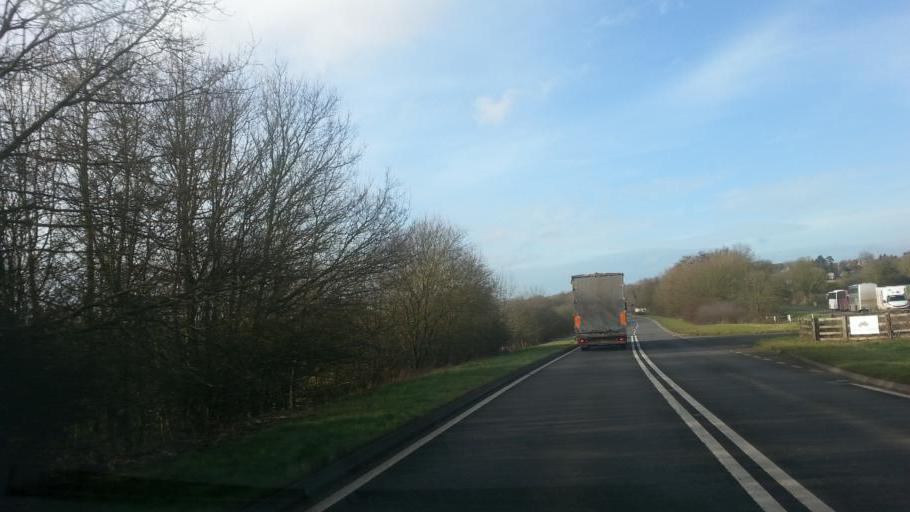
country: GB
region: England
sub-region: District of Rutland
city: Ridlington
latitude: 52.5952
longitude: -0.7838
